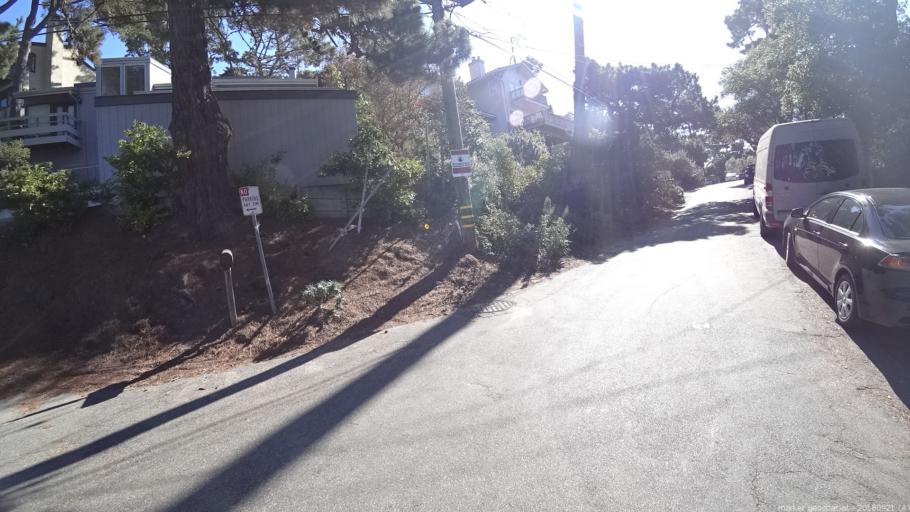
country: US
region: California
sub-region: Monterey County
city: Carmel-by-the-Sea
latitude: 36.5631
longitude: -121.9148
